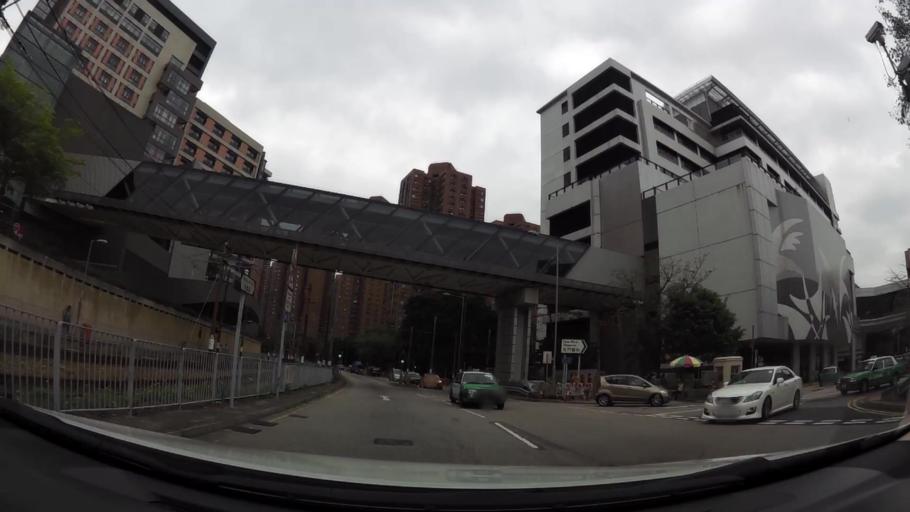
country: HK
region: Tuen Mun
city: Tuen Mun
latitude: 22.4091
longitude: 113.9759
